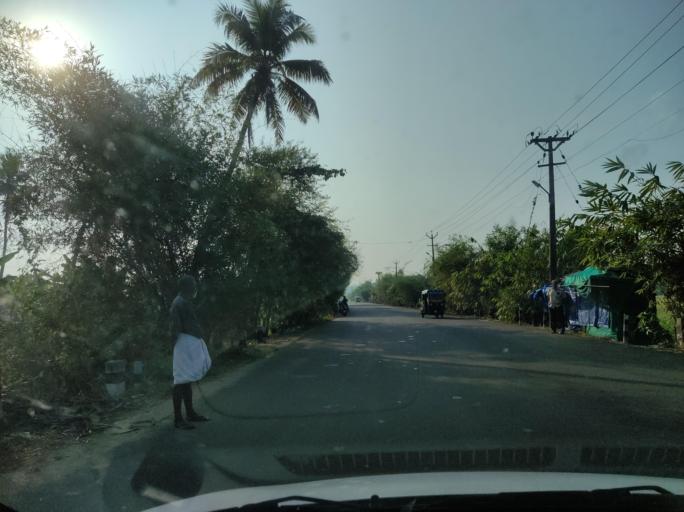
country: IN
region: Kerala
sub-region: Kottayam
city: Kottayam
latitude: 9.5686
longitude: 76.5035
